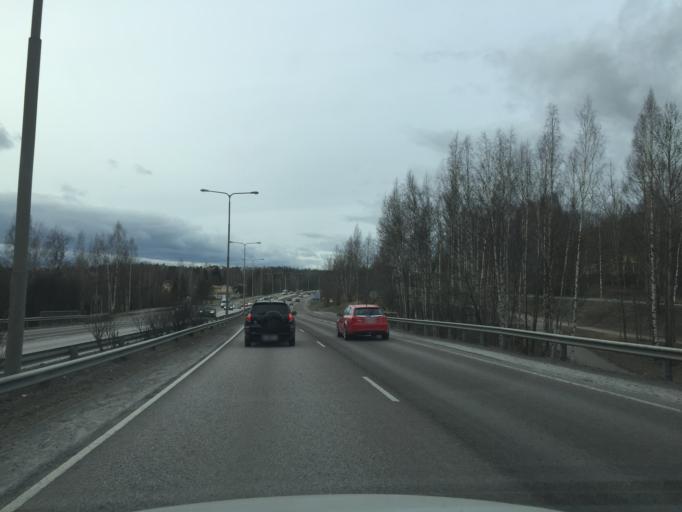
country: FI
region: Uusimaa
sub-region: Helsinki
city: Teekkarikylae
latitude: 60.2730
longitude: 24.8733
